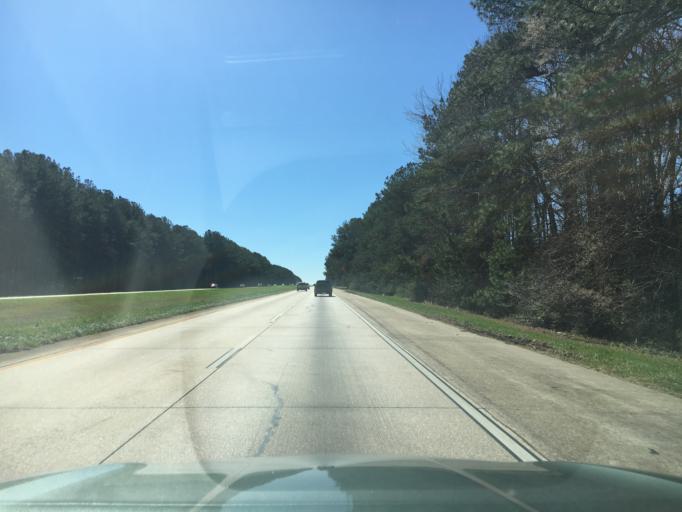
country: US
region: Georgia
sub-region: Troup County
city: Hogansville
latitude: 33.1263
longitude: -84.8948
